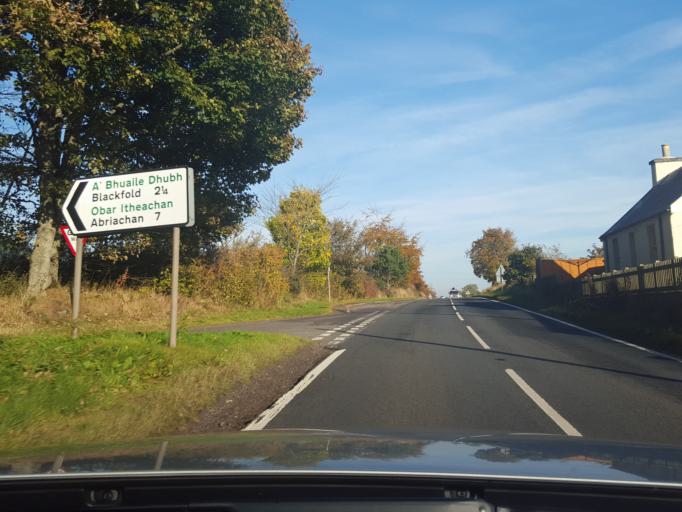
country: GB
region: Scotland
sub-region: Highland
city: Inverness
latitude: 57.4445
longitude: -4.2943
